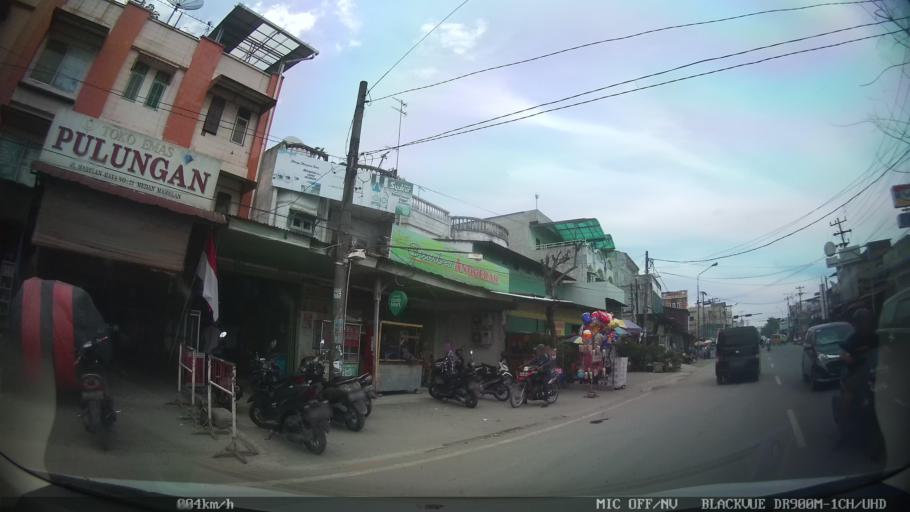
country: ID
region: North Sumatra
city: Labuhan Deli
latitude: 3.7101
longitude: 98.6606
